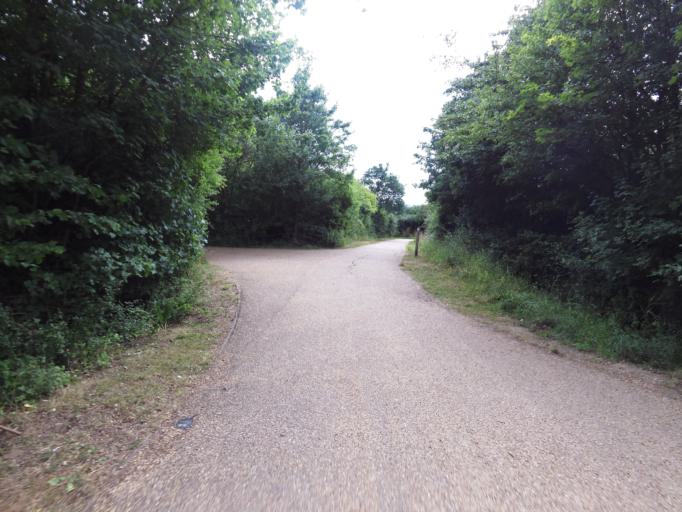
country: GB
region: England
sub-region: Essex
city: Colchester
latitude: 51.9054
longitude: 0.9134
